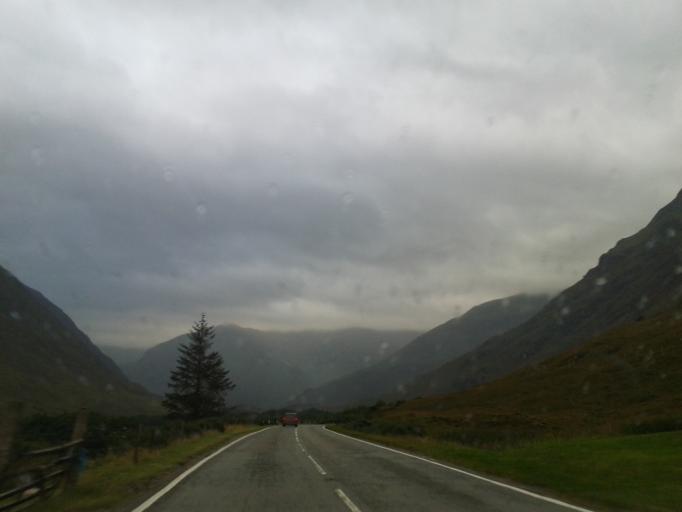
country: GB
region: Scotland
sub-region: Highland
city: Fort William
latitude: 57.1952
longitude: -5.3889
